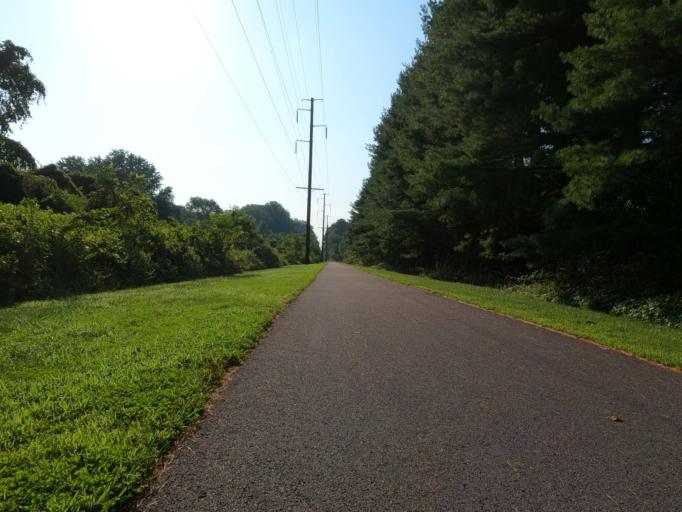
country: US
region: Maryland
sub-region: Anne Arundel County
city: Gambrills
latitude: 39.0556
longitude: -76.6462
